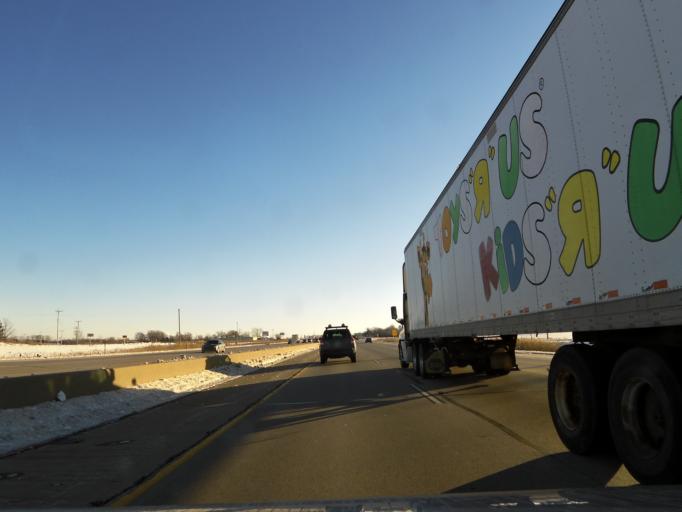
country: US
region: Wisconsin
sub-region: Kenosha County
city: Somers
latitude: 42.6483
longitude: -87.9530
